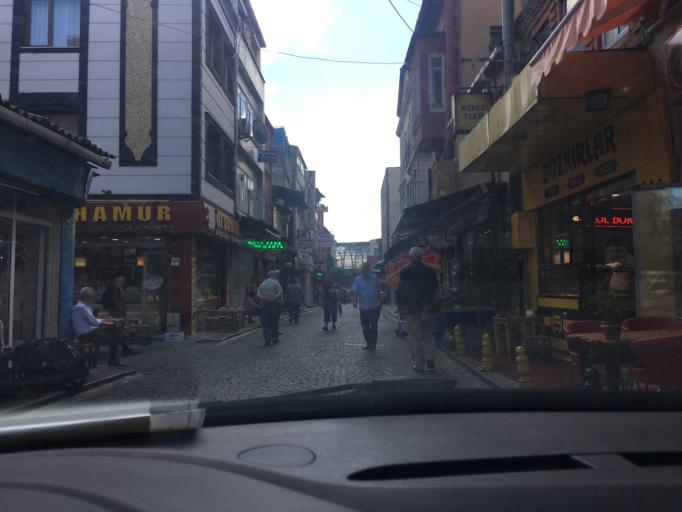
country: TR
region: Istanbul
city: Eminoenue
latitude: 41.0200
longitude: 28.9622
